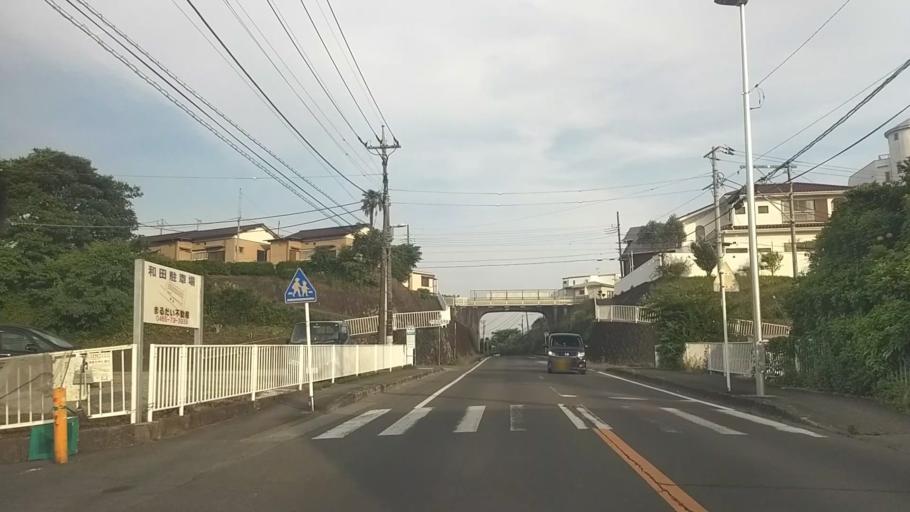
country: JP
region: Kanagawa
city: Odawara
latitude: 35.3127
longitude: 139.1170
